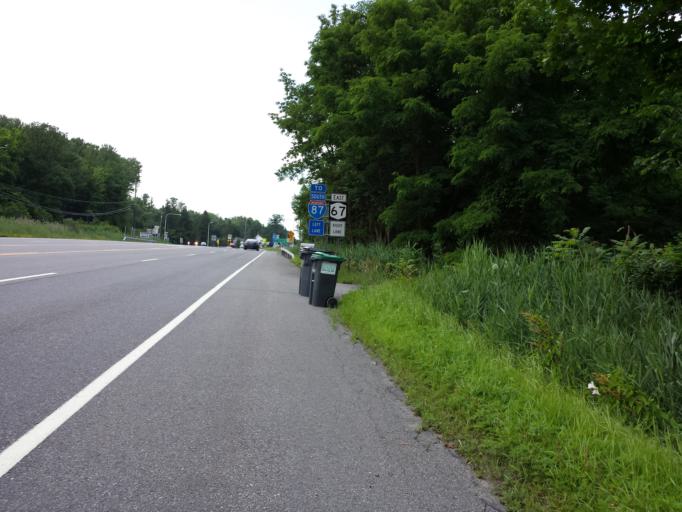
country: US
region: New York
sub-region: Saratoga County
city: Country Knolls
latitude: 42.9462
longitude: -73.7897
